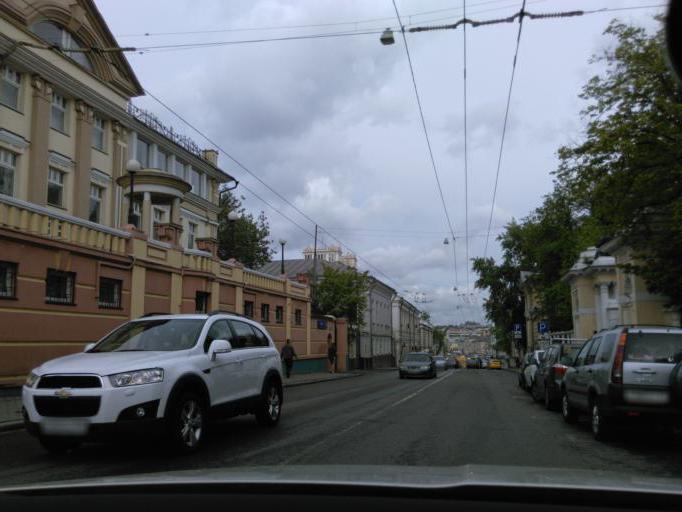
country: RU
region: Moscow
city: Zamoskvorech'ye
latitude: 55.7461
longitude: 37.6482
